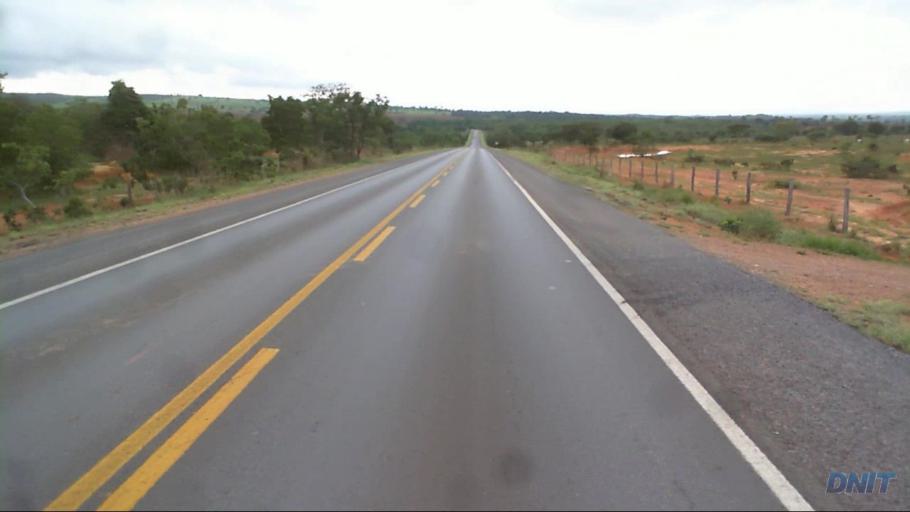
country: BR
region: Goias
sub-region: Padre Bernardo
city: Padre Bernardo
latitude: -15.2136
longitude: -48.5596
